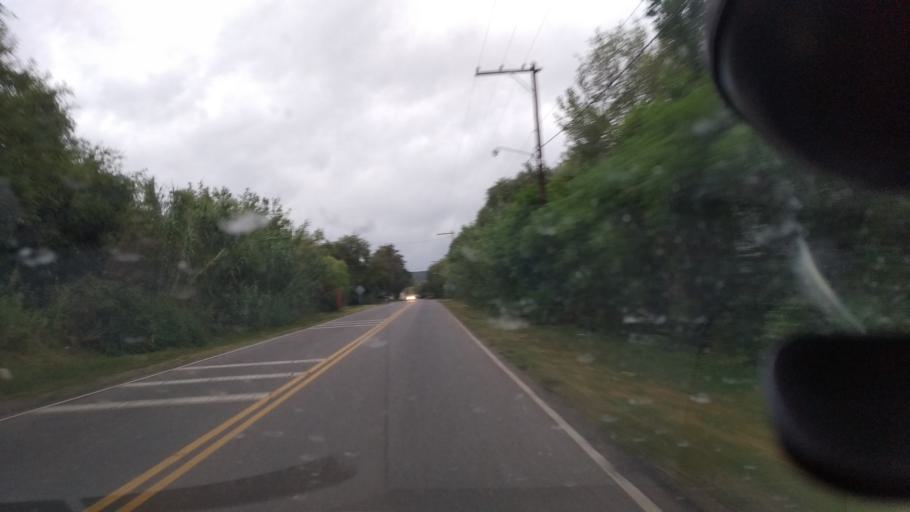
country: AR
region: Cordoba
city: Villa Las Rosas
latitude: -31.9363
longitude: -65.0414
